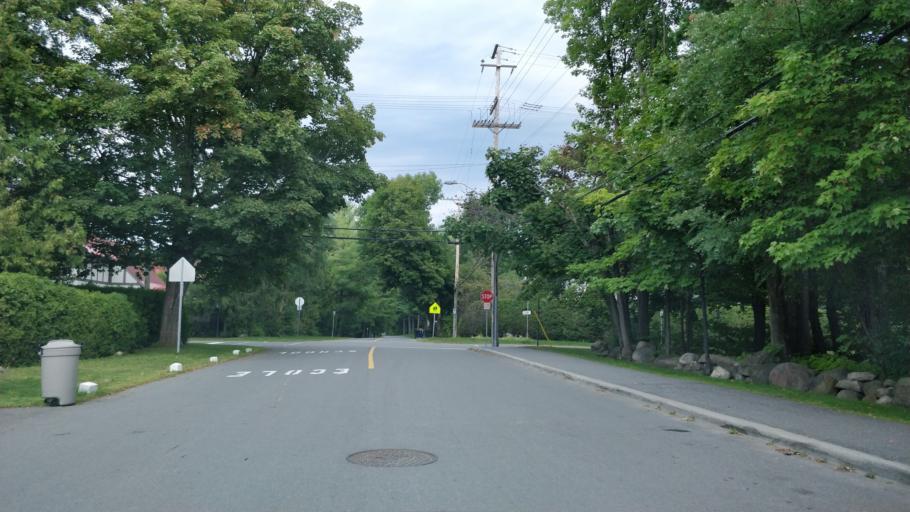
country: CA
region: Quebec
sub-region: Outaouais
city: Gatineau
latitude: 45.4506
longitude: -75.6791
